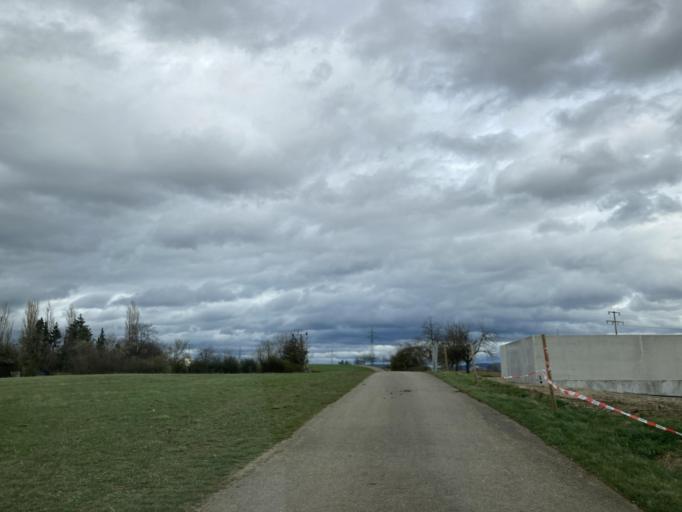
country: DE
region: Baden-Wuerttemberg
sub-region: Tuebingen Region
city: Gomaringen
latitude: 48.4802
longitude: 9.1189
